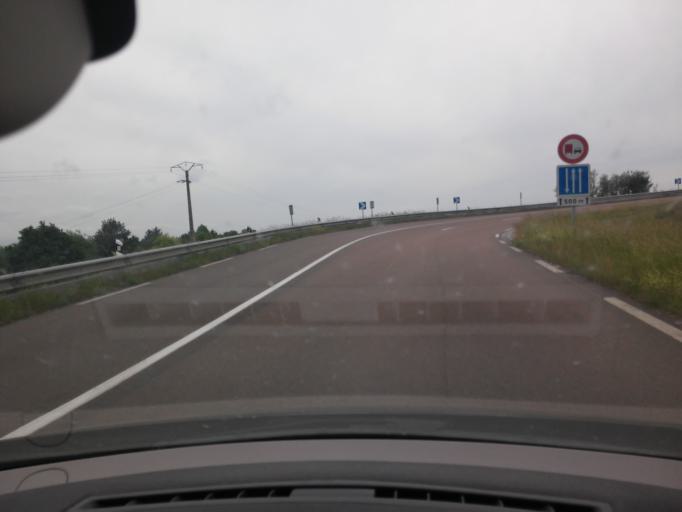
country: FR
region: Lorraine
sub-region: Departement de la Meuse
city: Saint-Mihiel
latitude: 48.8715
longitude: 5.5222
